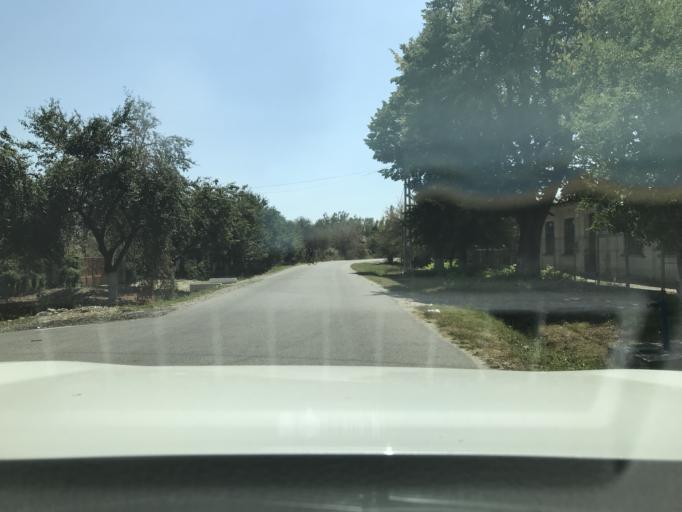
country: RO
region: Olt
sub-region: Comuna Falcoiu
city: Falcoiu
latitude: 44.2386
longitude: 24.3666
